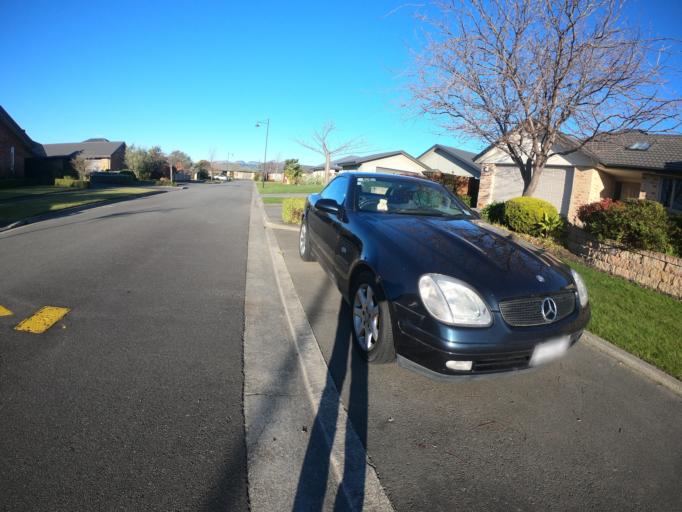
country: NZ
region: Canterbury
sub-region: Selwyn District
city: Prebbleton
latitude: -43.5682
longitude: 172.5672
